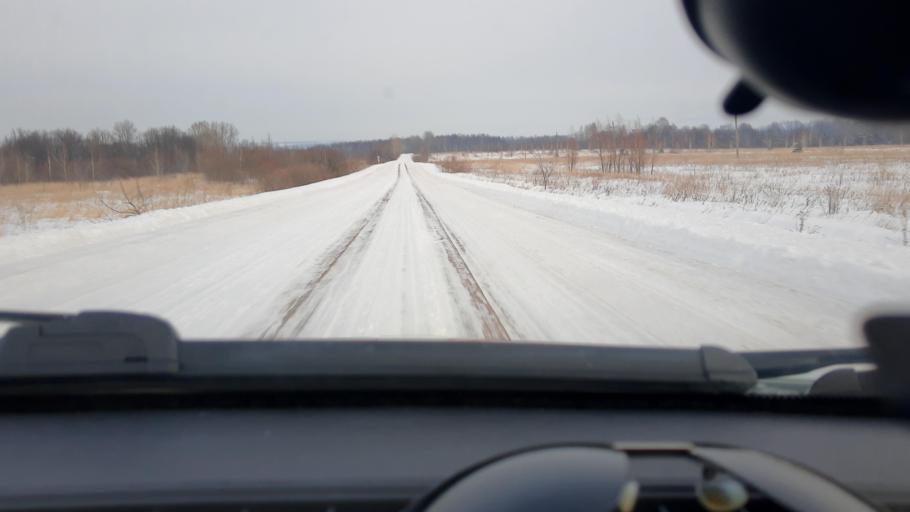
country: RU
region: Bashkortostan
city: Yazykovo
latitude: 55.0396
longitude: 56.2922
